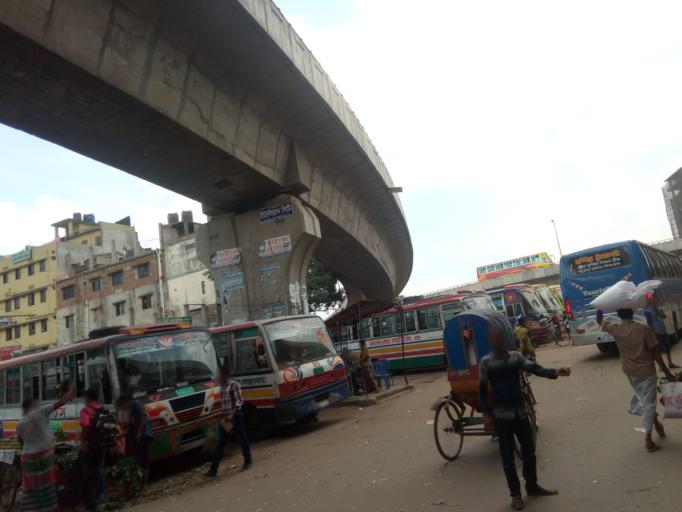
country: BD
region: Dhaka
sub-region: Dhaka
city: Dhaka
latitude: 23.7148
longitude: 90.4252
